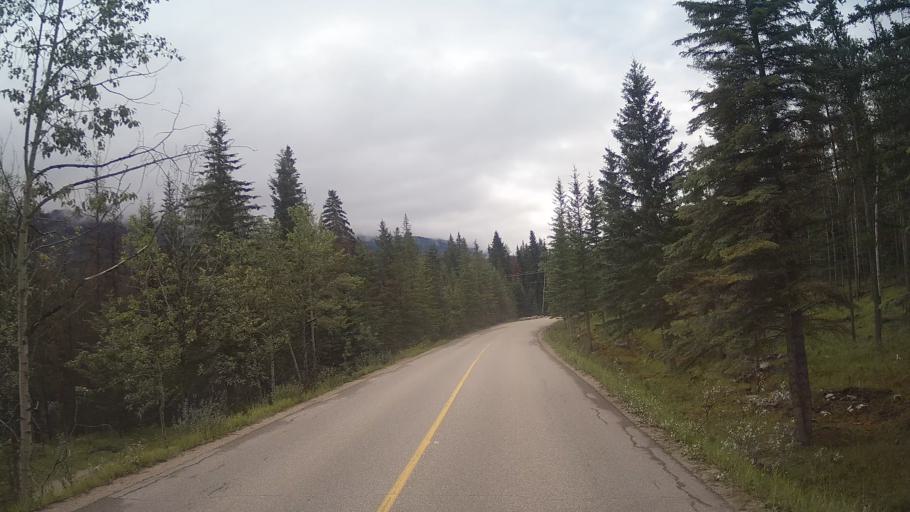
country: CA
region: Alberta
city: Jasper Park Lodge
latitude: 52.8679
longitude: -118.0729
